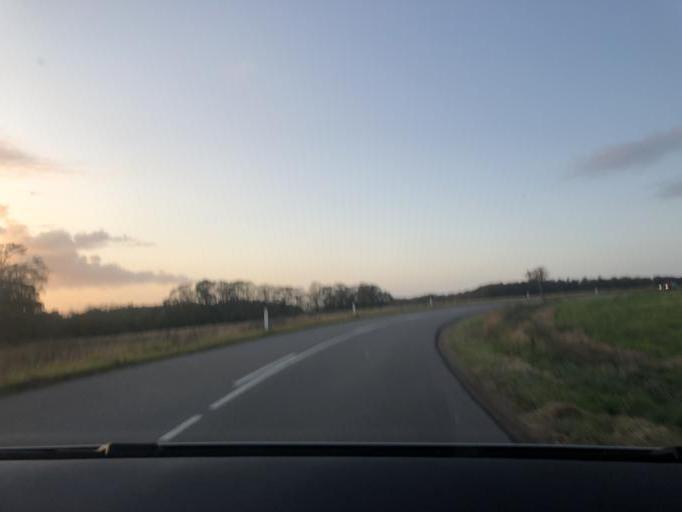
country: DK
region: Capital Region
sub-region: Egedal Kommune
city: Stenlose
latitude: 55.8028
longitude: 12.2121
